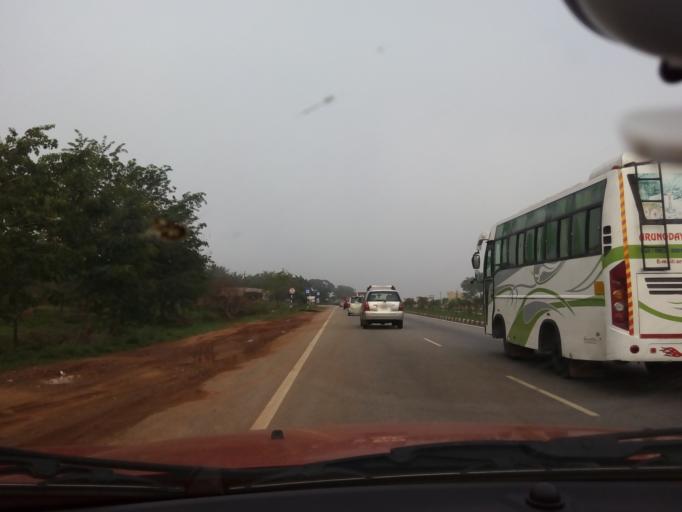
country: IN
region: Karnataka
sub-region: Tumkur
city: Kunigal
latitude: 13.0361
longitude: 77.0957
